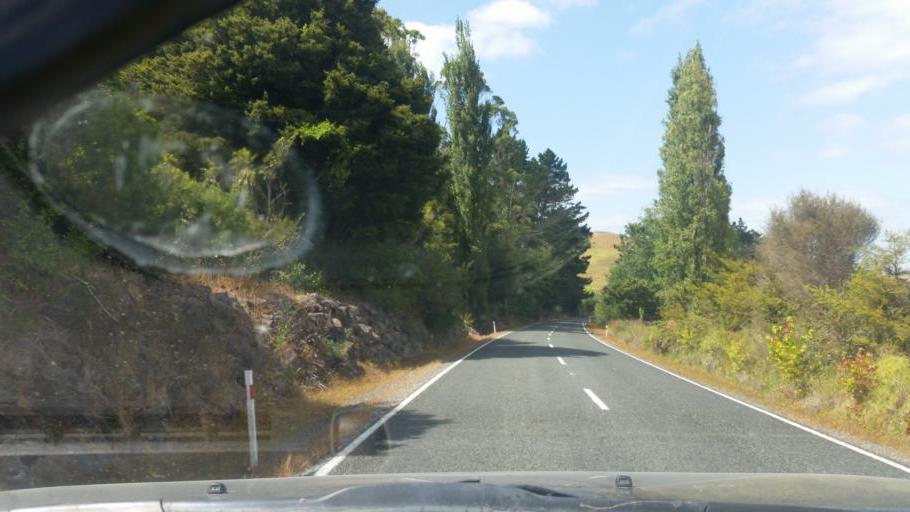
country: NZ
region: Northland
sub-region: Whangarei
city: Ruakaka
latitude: -35.9471
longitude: 174.2931
